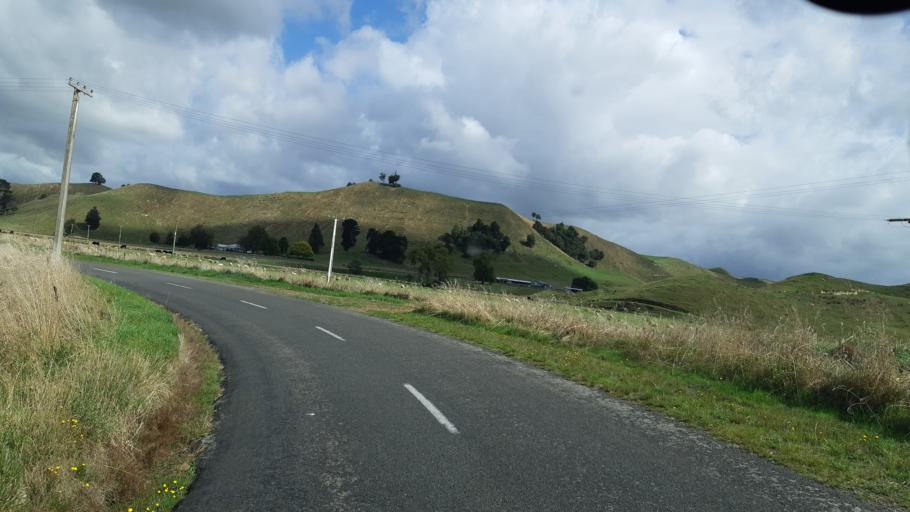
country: NZ
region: Manawatu-Wanganui
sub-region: Rangitikei District
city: Bulls
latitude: -39.8865
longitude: 175.6086
